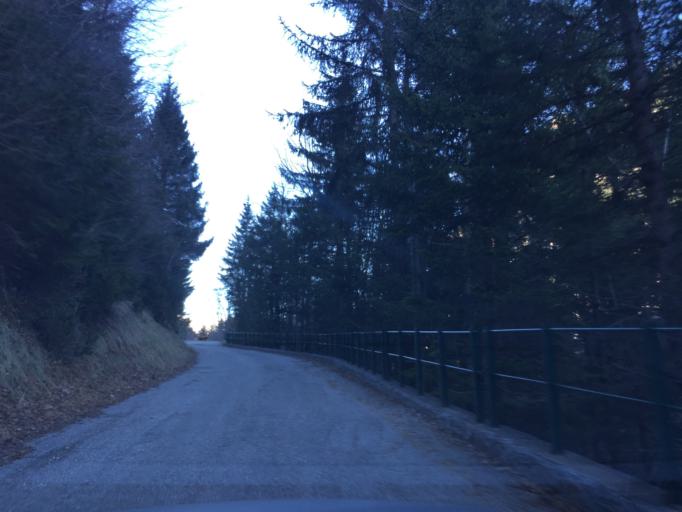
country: FR
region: Rhone-Alpes
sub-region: Departement de la Savoie
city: Courchevel
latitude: 45.3935
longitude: 6.7106
